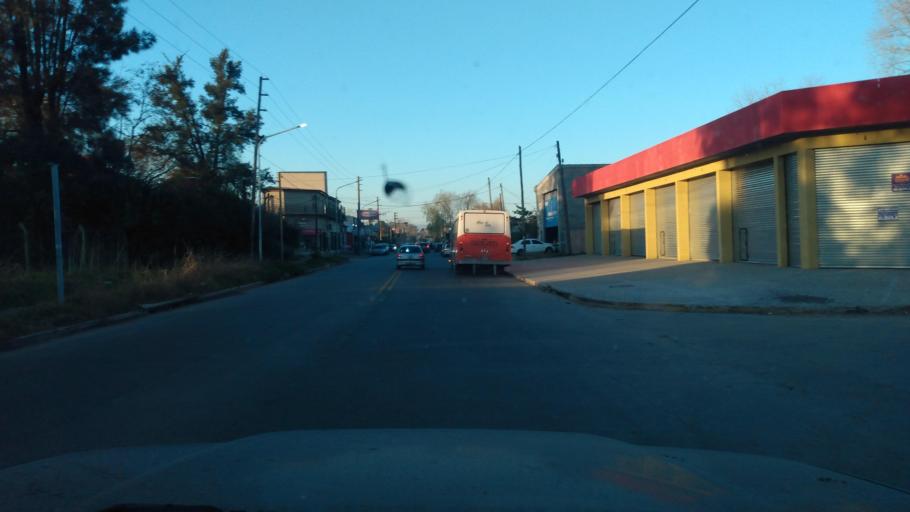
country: AR
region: Buenos Aires
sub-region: Partido de General Rodriguez
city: General Rodriguez
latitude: -34.5997
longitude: -58.9437
